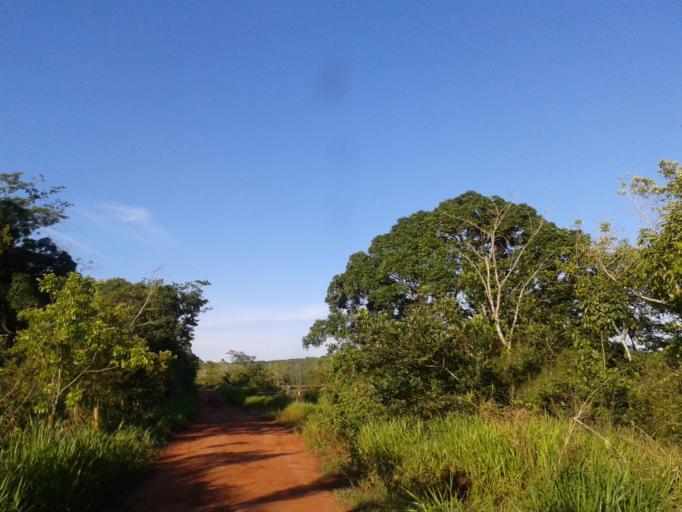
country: BR
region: Minas Gerais
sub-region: Santa Vitoria
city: Santa Vitoria
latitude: -18.9619
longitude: -49.8689
